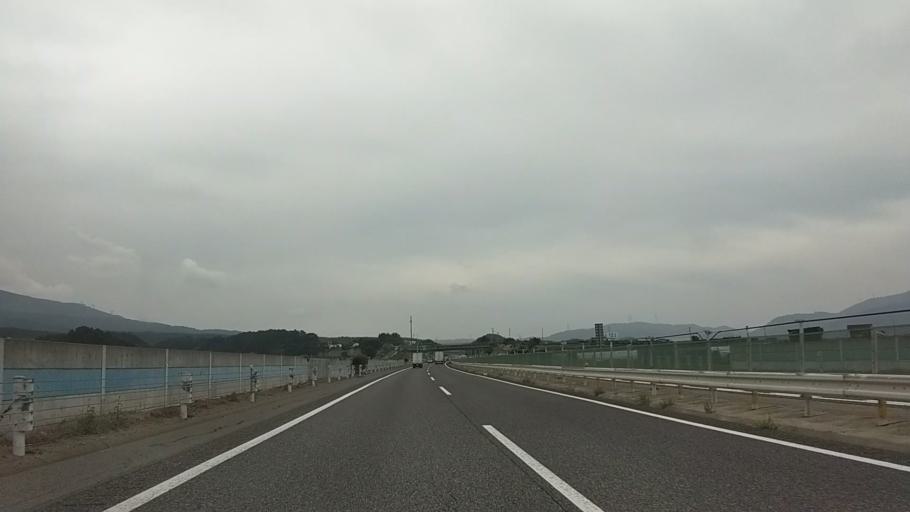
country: JP
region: Nagano
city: Shiojiri
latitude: 36.1296
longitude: 137.9745
